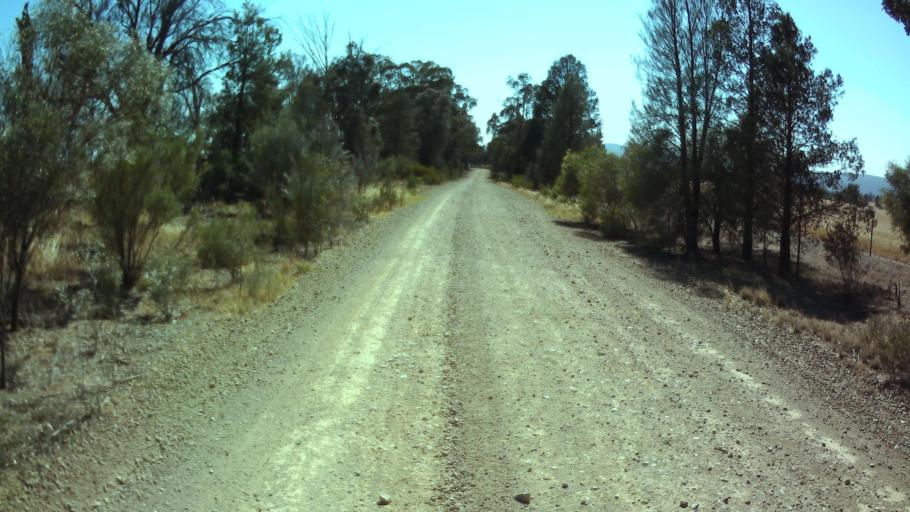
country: AU
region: New South Wales
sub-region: Weddin
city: Grenfell
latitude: -33.9041
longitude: 147.8596
